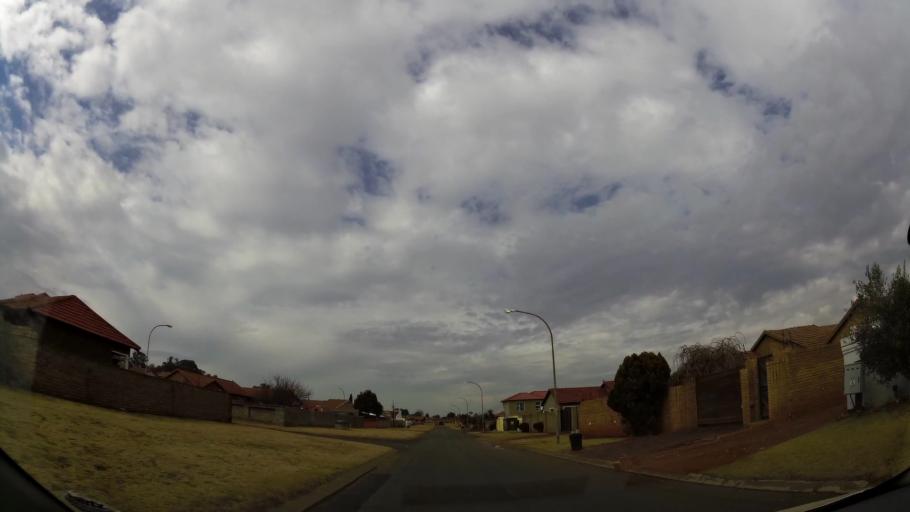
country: ZA
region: Gauteng
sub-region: Ekurhuleni Metropolitan Municipality
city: Germiston
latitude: -26.3160
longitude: 28.1746
